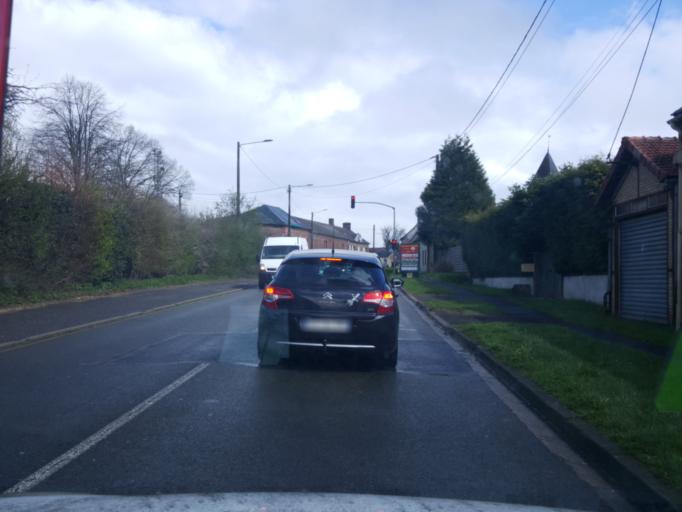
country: FR
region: Picardie
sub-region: Departement de l'Oise
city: Auneuil
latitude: 49.3543
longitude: 1.9412
